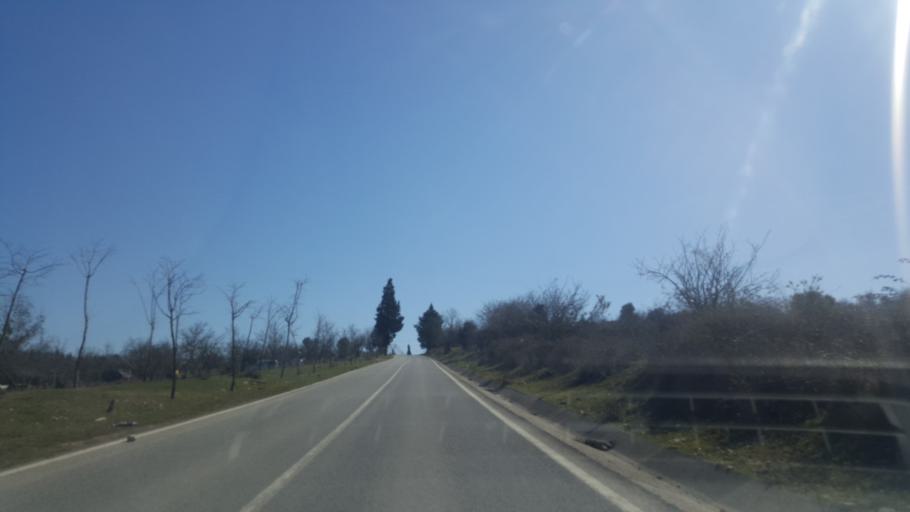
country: TR
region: Kocaeli
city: Tavsancil
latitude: 40.7863
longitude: 29.5726
